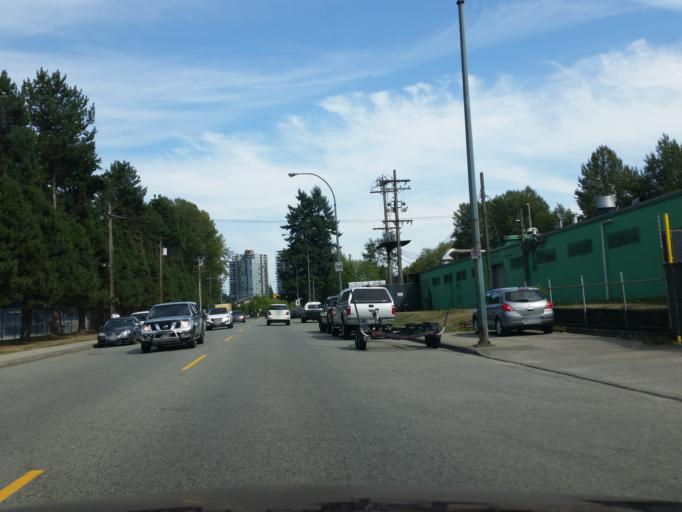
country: CA
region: British Columbia
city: Port Moody
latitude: 49.2788
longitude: -122.8437
